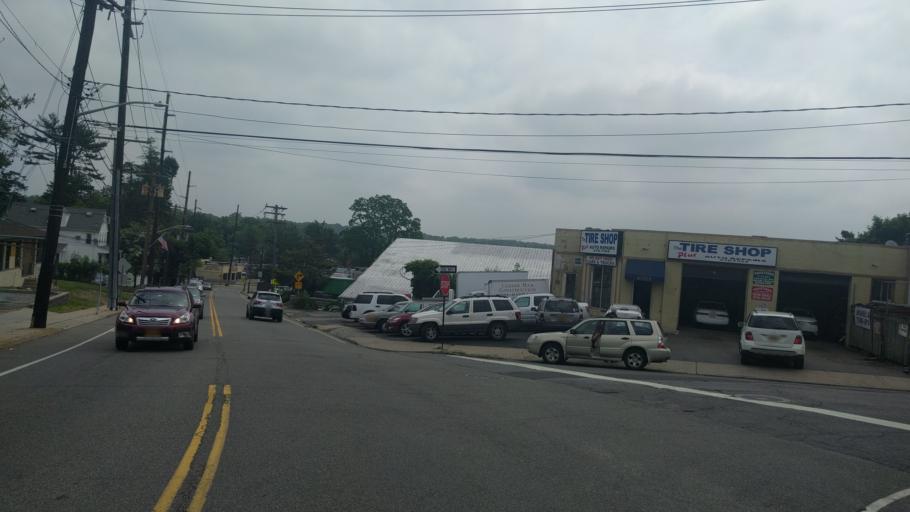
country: US
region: New York
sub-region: Nassau County
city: Glen Head
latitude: 40.8339
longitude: -73.6261
